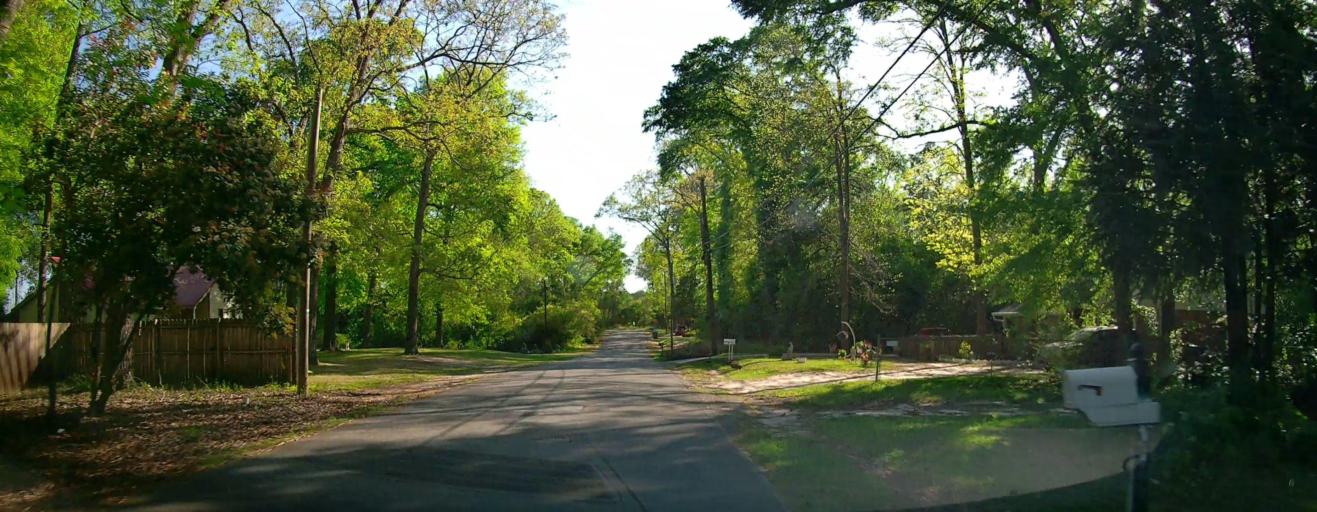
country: US
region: Georgia
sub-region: Houston County
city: Perry
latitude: 32.4517
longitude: -83.7549
